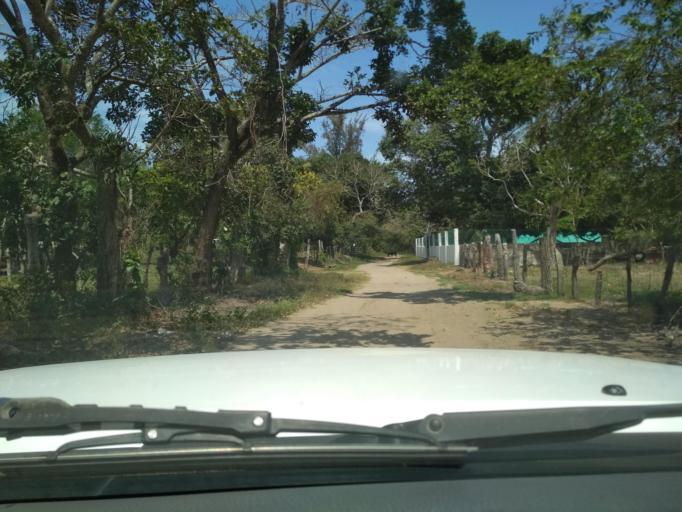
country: MX
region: Veracruz
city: Anton Lizardo
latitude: 19.0103
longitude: -95.9889
